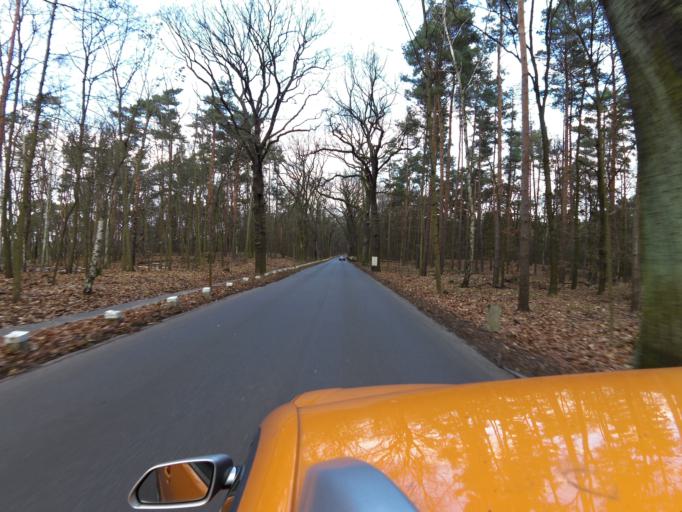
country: DE
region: Berlin
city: Gatow
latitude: 52.4815
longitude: 13.1972
